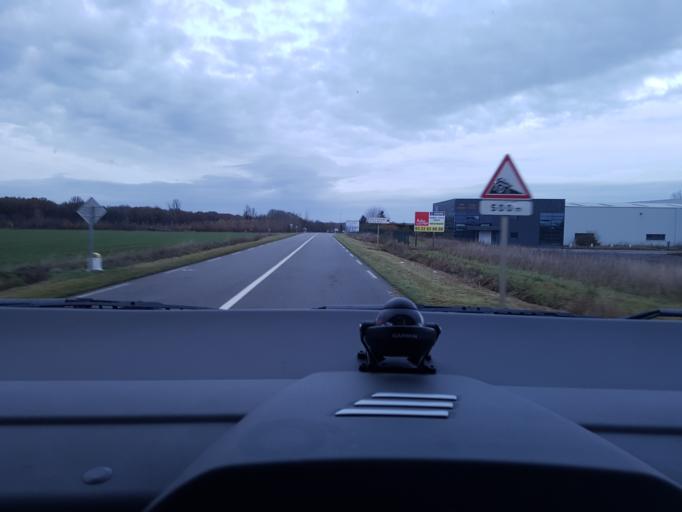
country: FR
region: Picardie
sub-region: Departement de la Somme
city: Poix-de-Picardie
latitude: 49.7630
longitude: 1.9720
